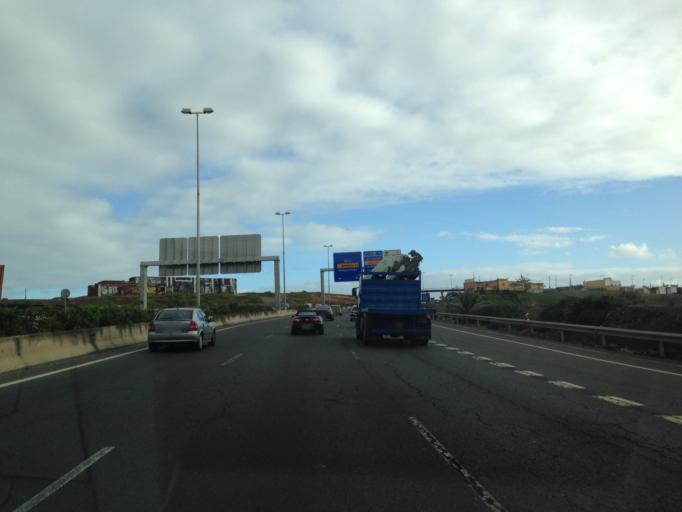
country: ES
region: Canary Islands
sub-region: Provincia de Las Palmas
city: Telde
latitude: 28.0223
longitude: -15.3883
